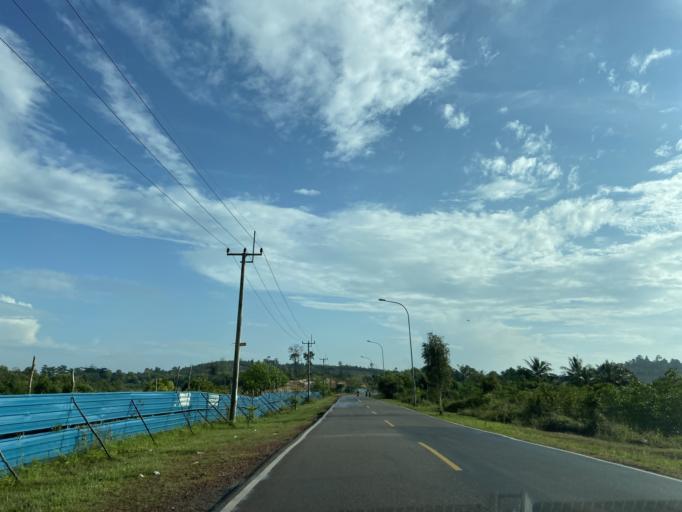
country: SG
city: Singapore
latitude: 0.9546
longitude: 104.0528
